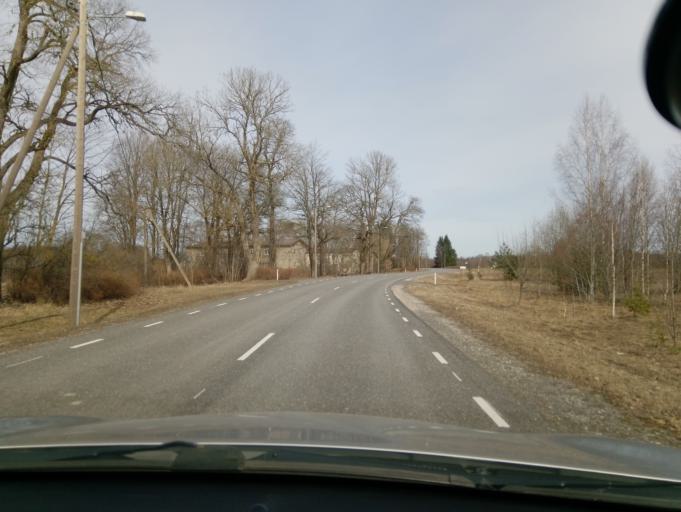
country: EE
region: Jaervamaa
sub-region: Tueri vald
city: Tueri
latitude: 58.8486
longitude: 25.3587
